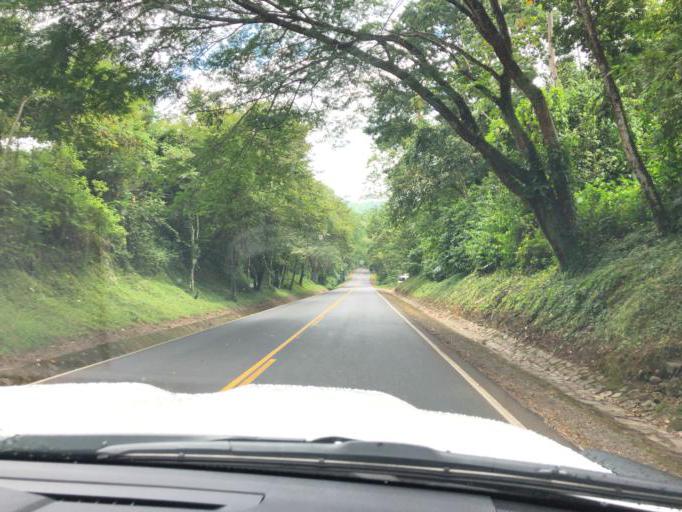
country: NI
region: Chontales
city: Villa Sandino
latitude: 11.9962
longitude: -84.9178
